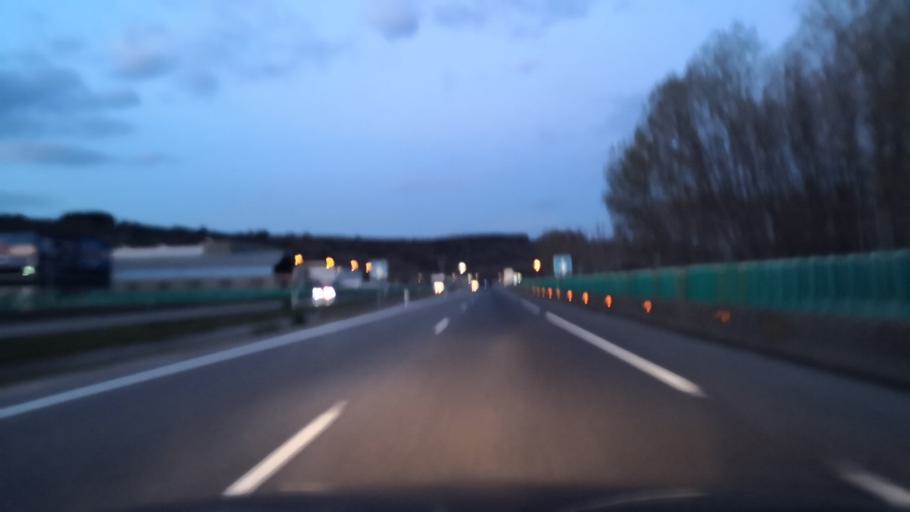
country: ES
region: Castille and Leon
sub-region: Provincia de Leon
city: Castropodame
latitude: 42.6195
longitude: -6.4594
